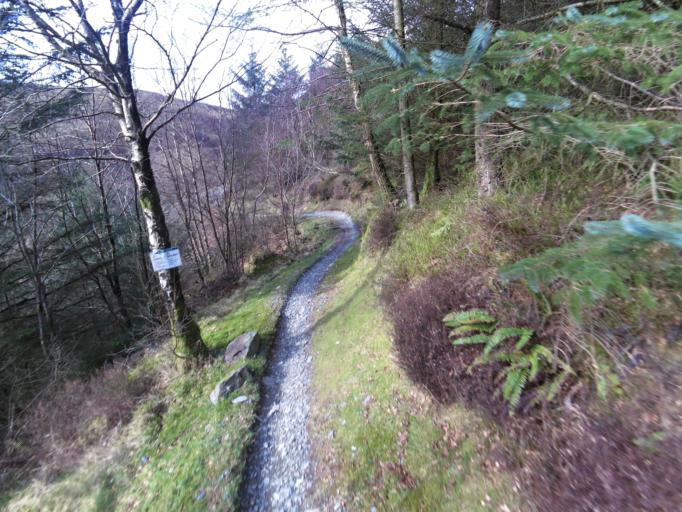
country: GB
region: Wales
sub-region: County of Ceredigion
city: Bow Street
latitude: 52.4271
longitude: -3.8875
